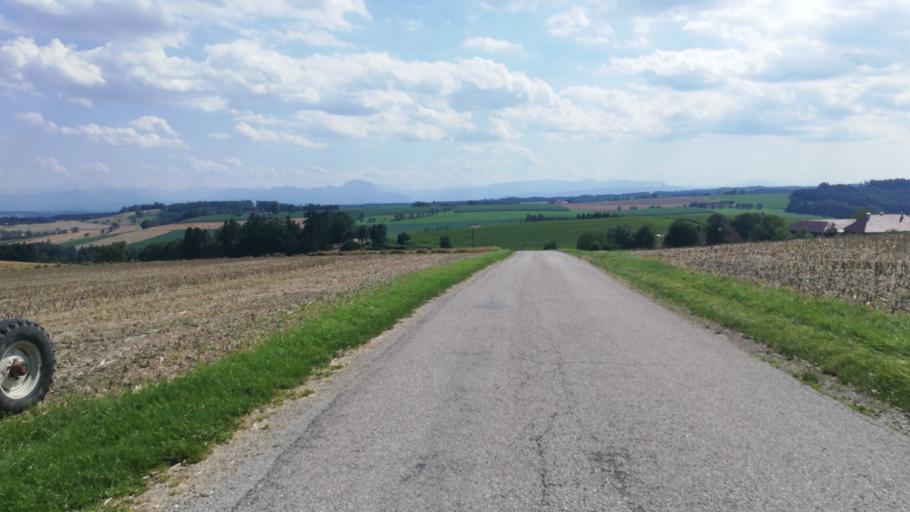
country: AT
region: Upper Austria
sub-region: Wels-Land
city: Pennewang
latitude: 48.1619
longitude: 13.8824
